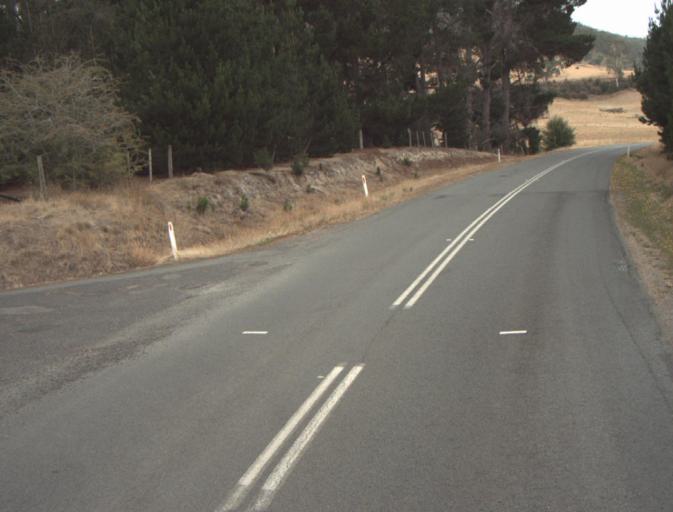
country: AU
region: Tasmania
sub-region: Northern Midlands
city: Evandale
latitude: -41.5045
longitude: 147.4819
